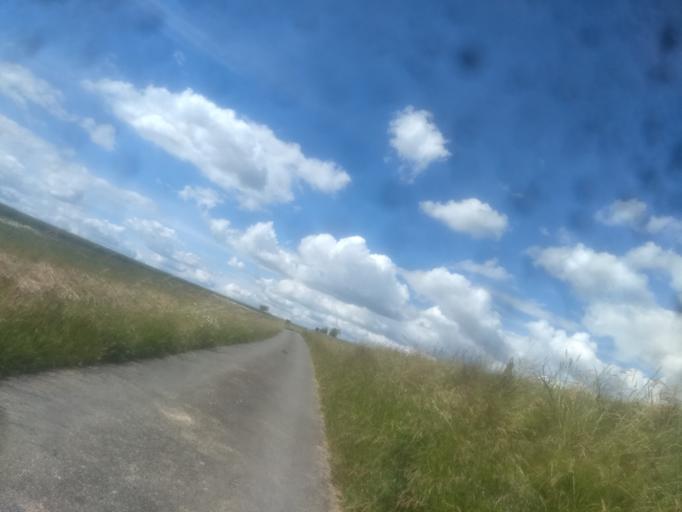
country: FR
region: Nord-Pas-de-Calais
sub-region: Departement du Pas-de-Calais
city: Tilloy-les-Mofflaines
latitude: 50.2336
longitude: 2.8360
